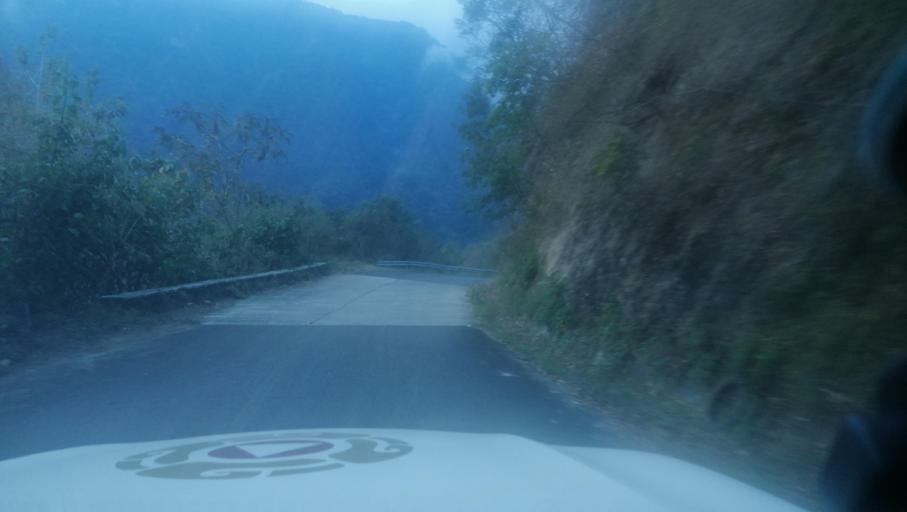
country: MX
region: Chiapas
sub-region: Cacahoatan
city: Benito Juarez
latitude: 15.1409
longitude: -92.1944
